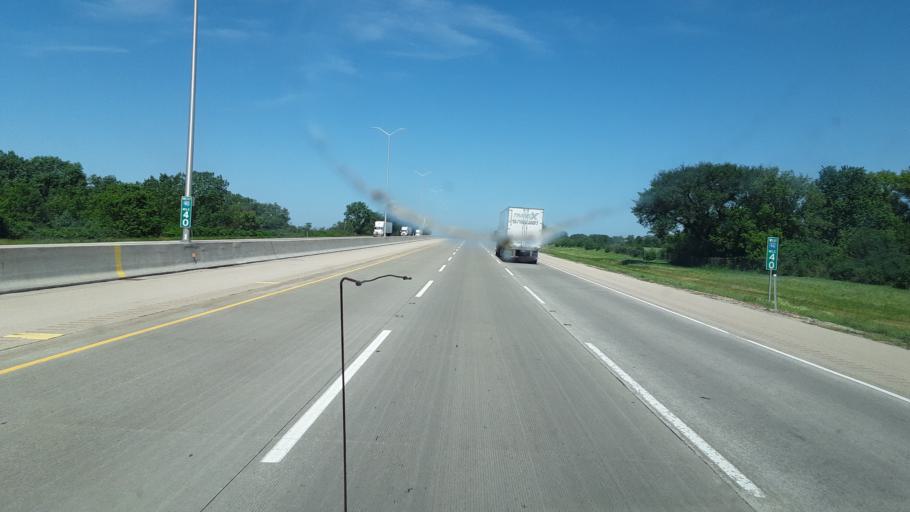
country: US
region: Illinois
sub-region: Kane County
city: Hampshire
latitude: 42.1564
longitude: -88.5506
